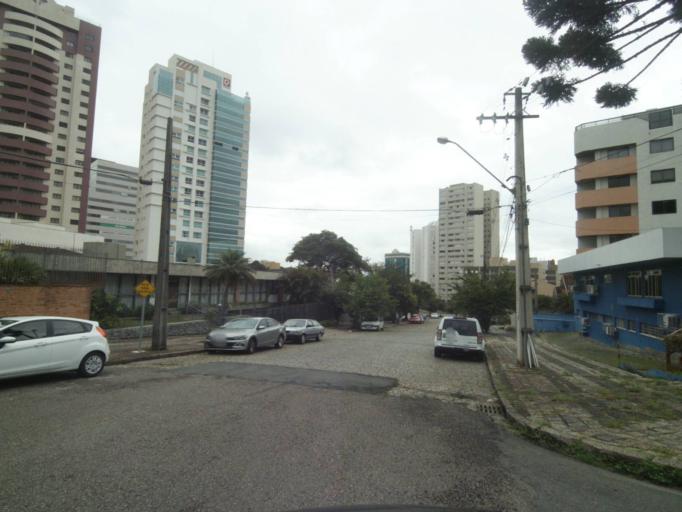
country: BR
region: Parana
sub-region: Curitiba
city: Curitiba
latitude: -25.4168
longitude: -49.2643
